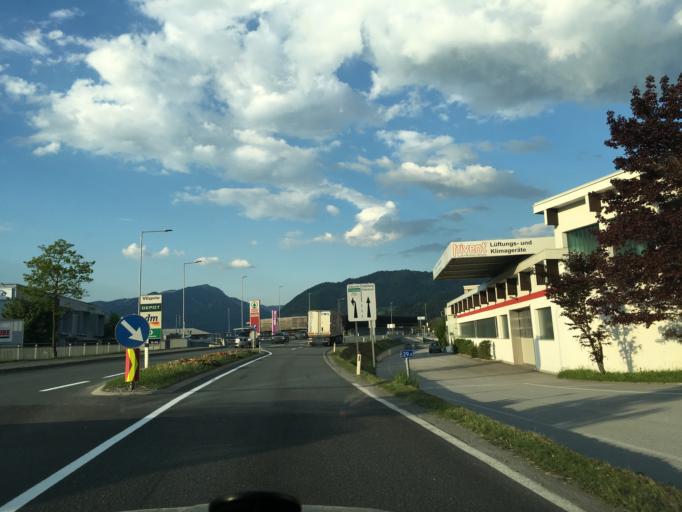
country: AT
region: Tyrol
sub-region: Politischer Bezirk Kitzbuhel
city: Sankt Johann in Tirol
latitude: 47.5282
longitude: 12.4256
